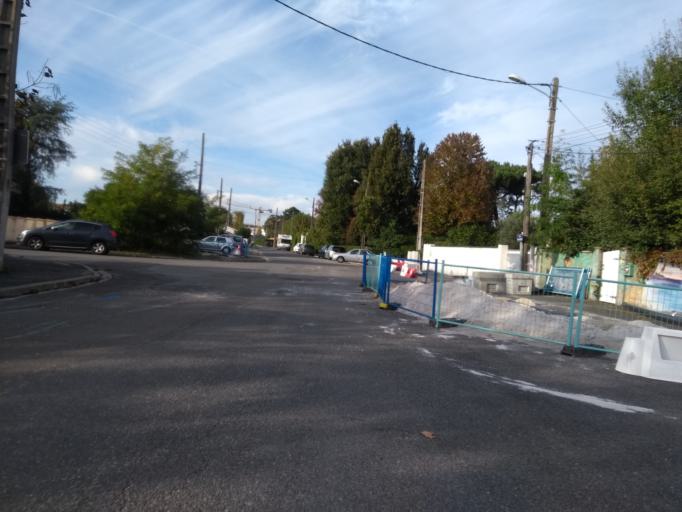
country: FR
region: Aquitaine
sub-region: Departement de la Gironde
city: Pessac
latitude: 44.7941
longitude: -0.6595
